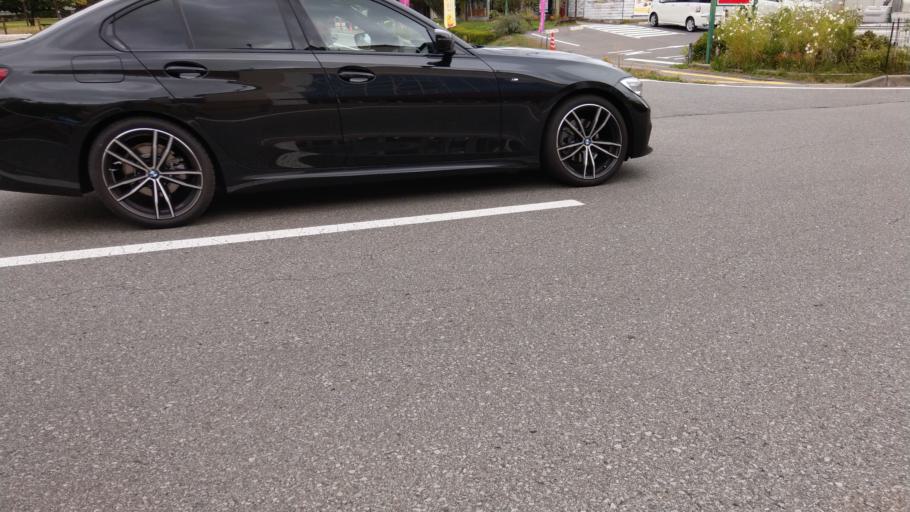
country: JP
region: Nagano
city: Komoro
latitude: 36.2762
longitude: 138.4642
